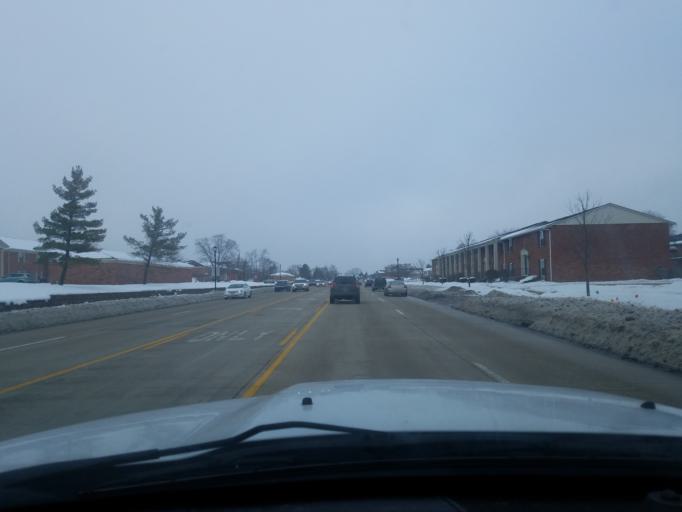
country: US
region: Indiana
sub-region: Saint Joseph County
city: Mishawaka
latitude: 41.6875
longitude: -86.1816
